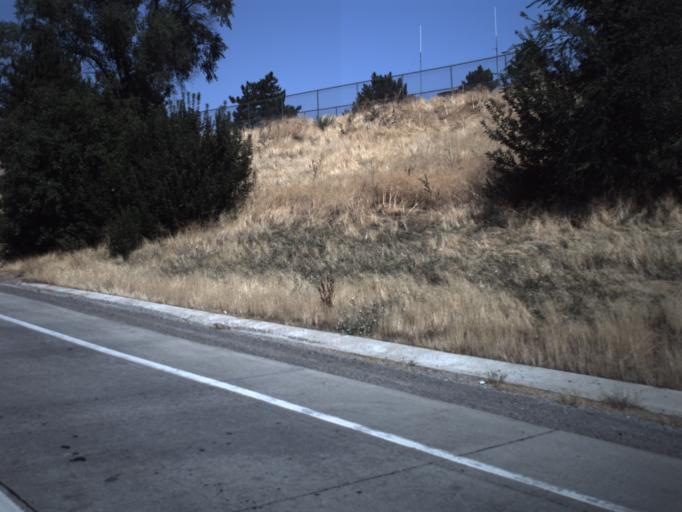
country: US
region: Utah
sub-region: Salt Lake County
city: Willard
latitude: 40.7209
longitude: -111.8517
